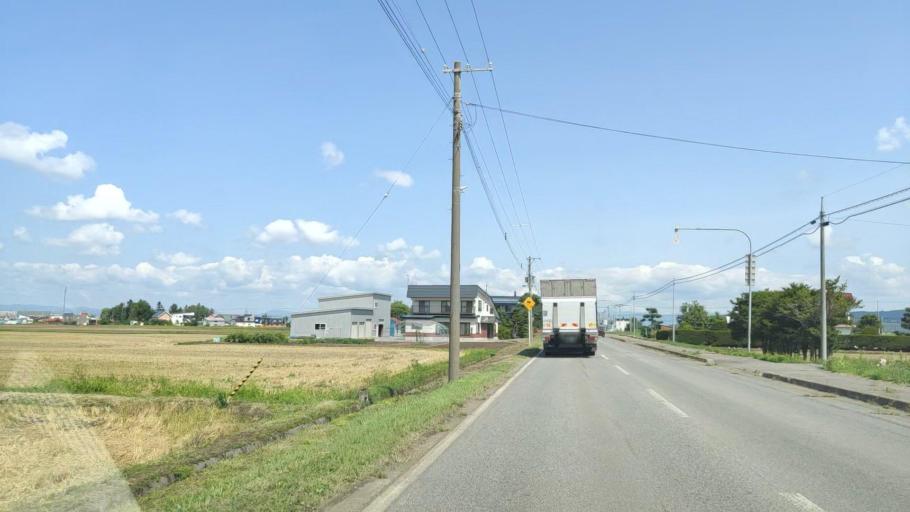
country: JP
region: Hokkaido
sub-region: Asahikawa-shi
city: Asahikawa
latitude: 43.7223
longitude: 142.4580
